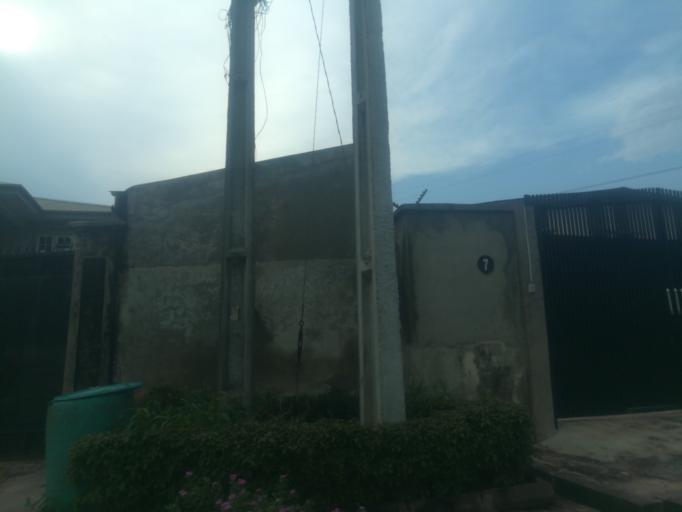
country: NG
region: Oyo
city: Ibadan
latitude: 7.3669
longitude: 3.8481
